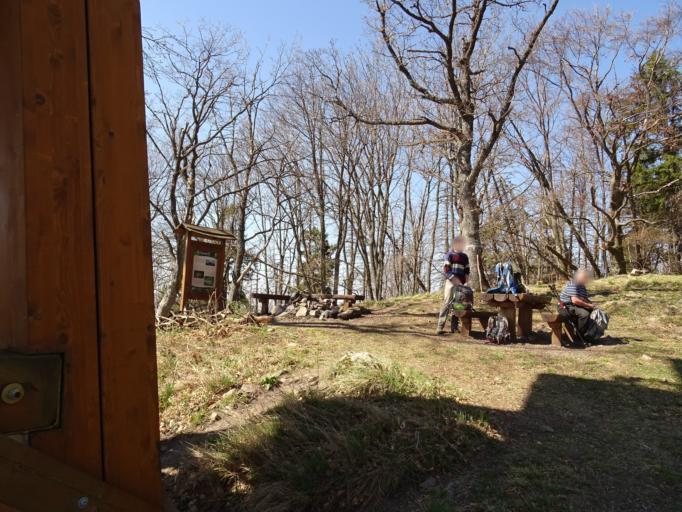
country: HU
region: Borsod-Abauj-Zemplen
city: Gonc
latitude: 48.5733
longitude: 21.4609
